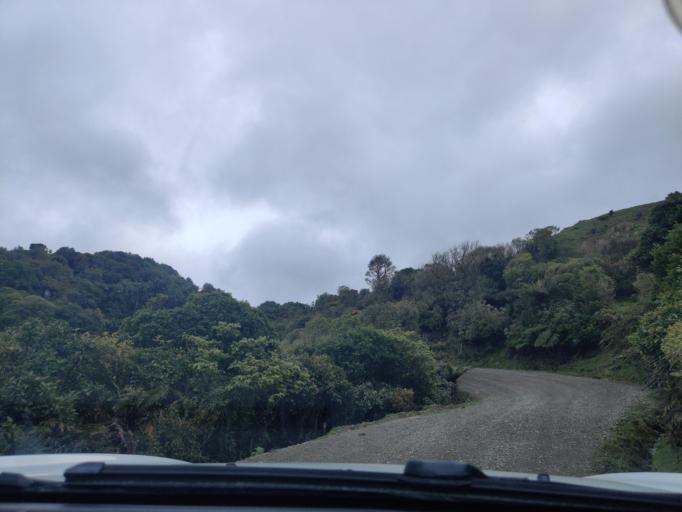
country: NZ
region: Manawatu-Wanganui
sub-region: Palmerston North City
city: Palmerston North
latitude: -40.2731
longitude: 175.8496
